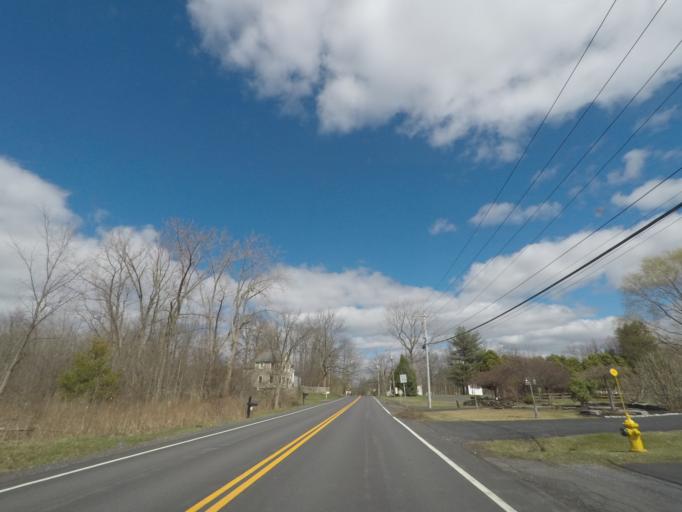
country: US
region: New York
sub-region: Albany County
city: Delmar
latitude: 42.5951
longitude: -73.8368
